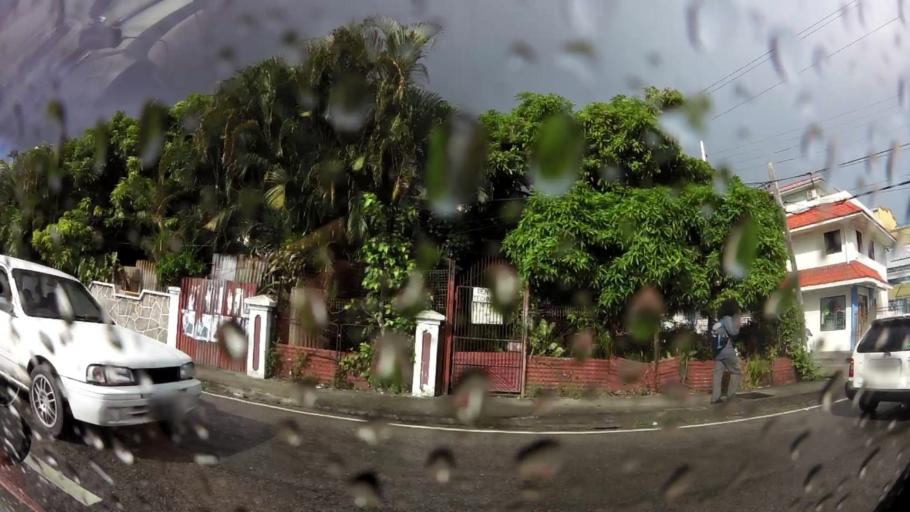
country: TT
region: Tunapuna/Piarco
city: Tunapuna
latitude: 10.6489
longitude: -61.4071
